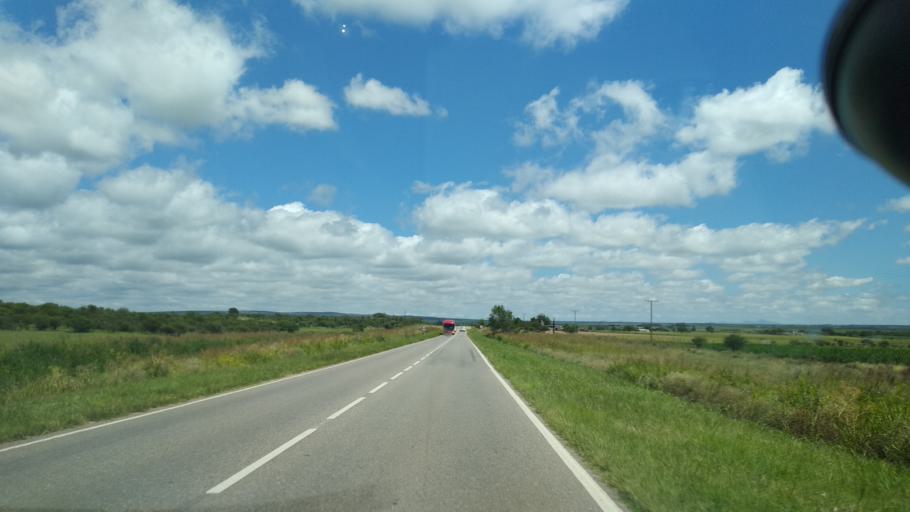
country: AR
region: Cordoba
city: Villa Cura Brochero
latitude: -31.6806
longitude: -65.0831
